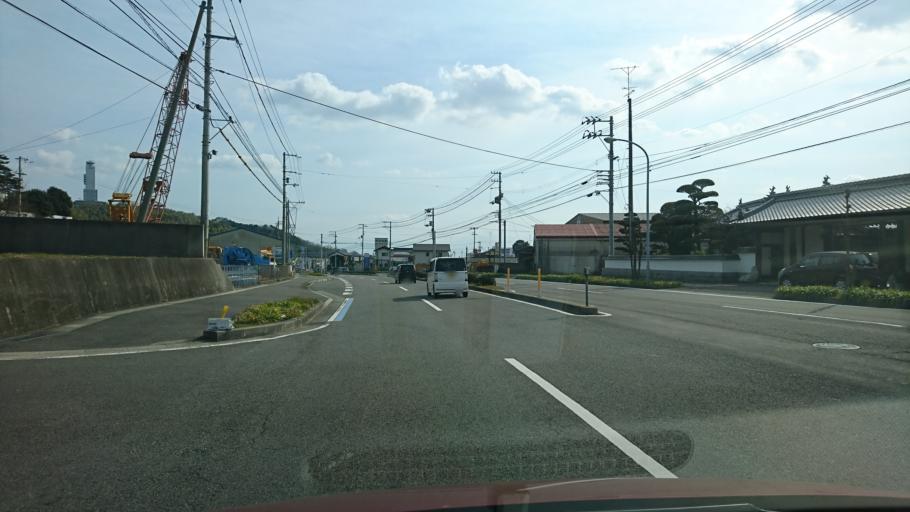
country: JP
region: Ehime
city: Hojo
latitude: 34.0913
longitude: 132.9804
